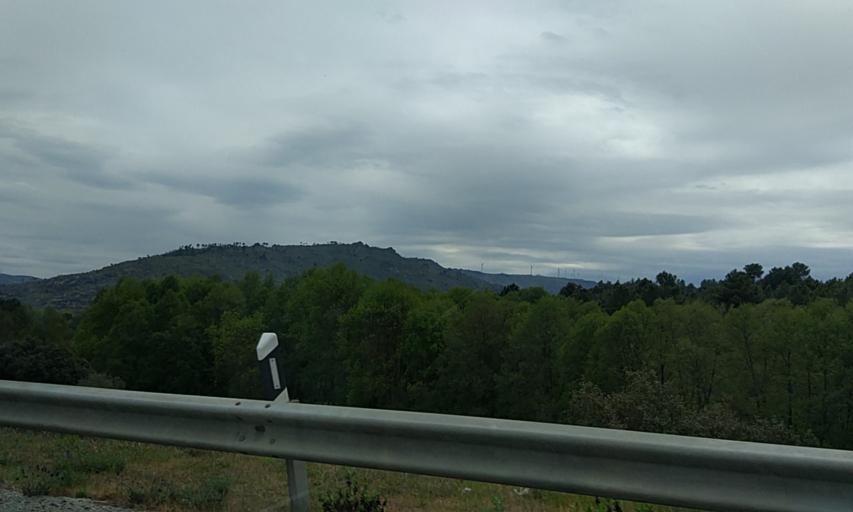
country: PT
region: Guarda
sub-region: Celorico da Beira
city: Celorico da Beira
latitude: 40.6367
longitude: -7.3216
